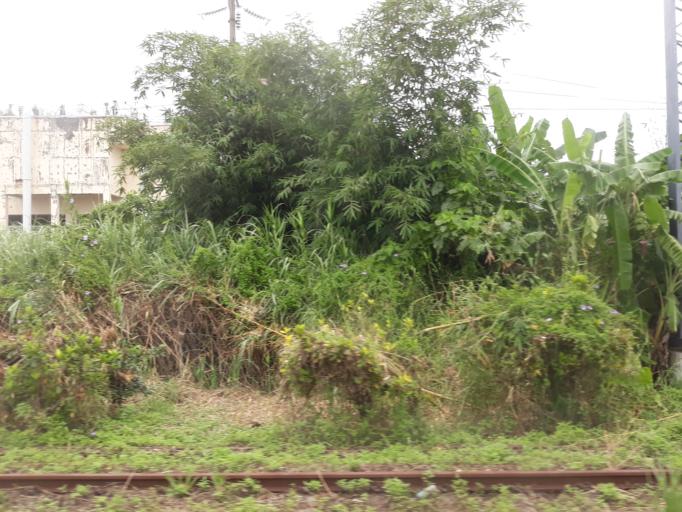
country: TW
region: Taiwan
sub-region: Yilan
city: Yilan
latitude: 24.6977
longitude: 121.7752
